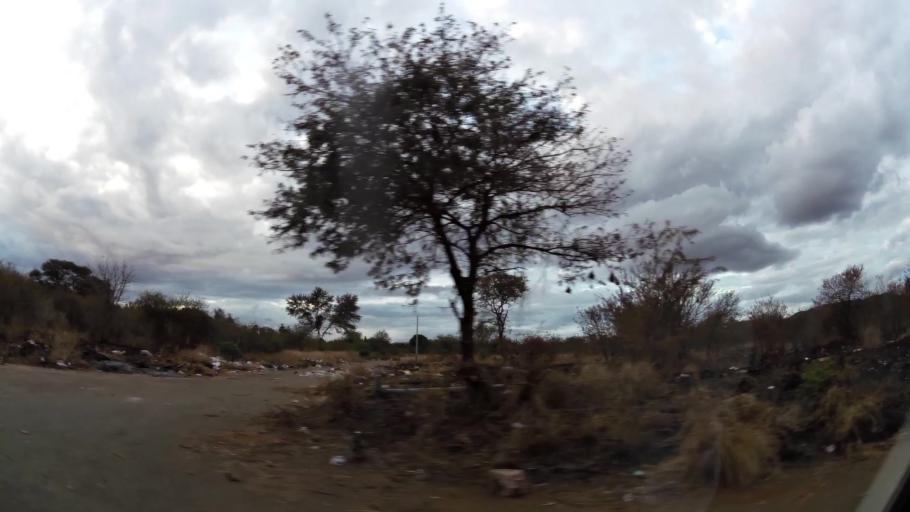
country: ZA
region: Limpopo
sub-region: Waterberg District Municipality
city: Mokopane
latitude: -24.1945
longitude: 28.9966
